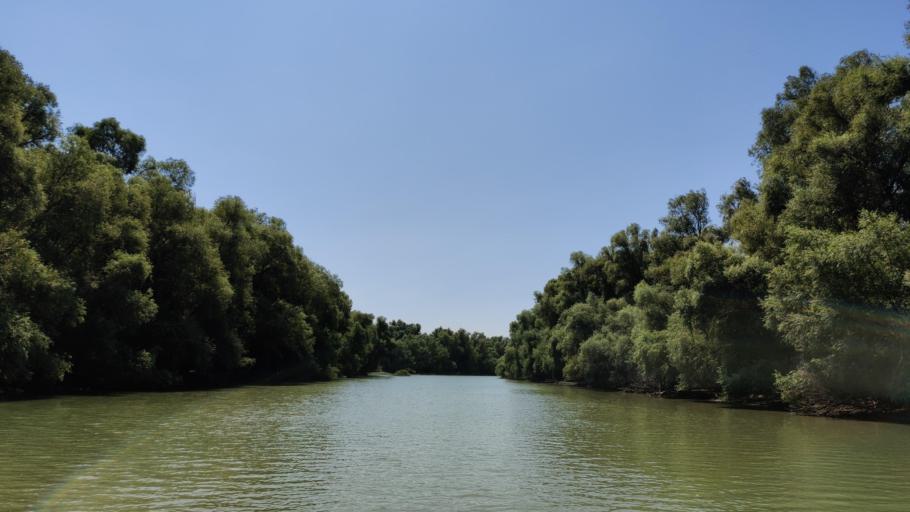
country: RO
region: Tulcea
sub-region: Comuna Pardina
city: Pardina
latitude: 45.2387
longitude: 28.9183
